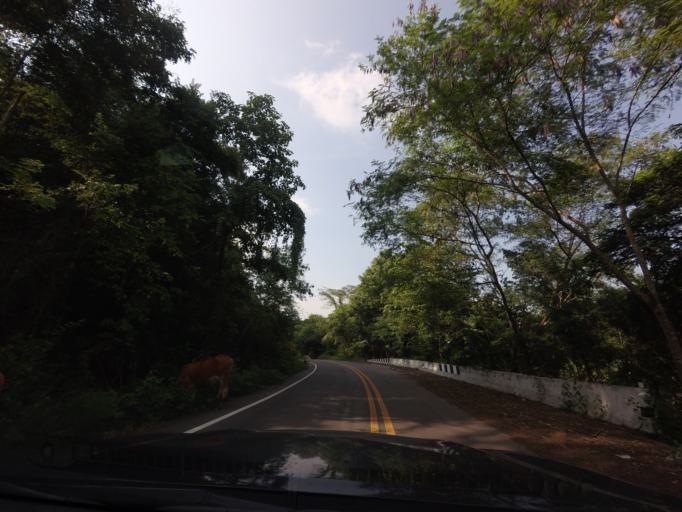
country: TH
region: Nan
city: Na Noi
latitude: 18.3527
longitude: 100.8803
